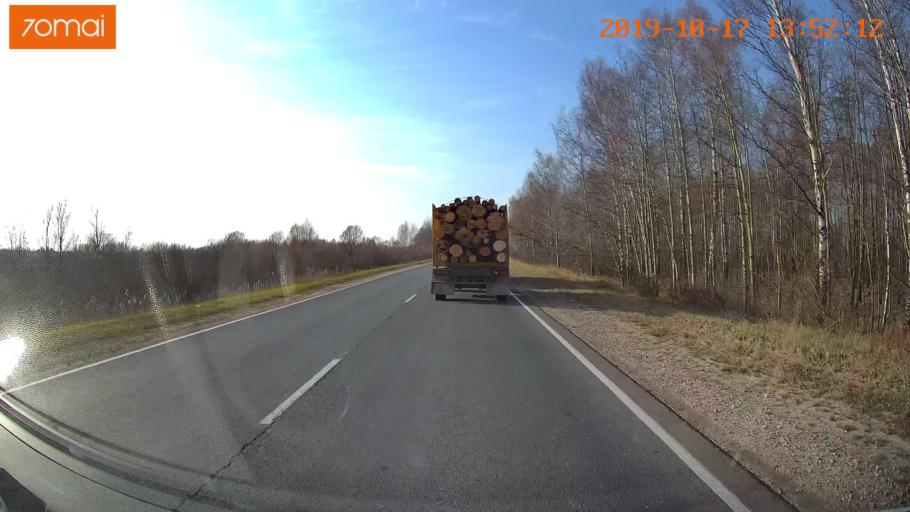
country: RU
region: Rjazan
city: Tuma
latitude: 55.1391
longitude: 40.3704
